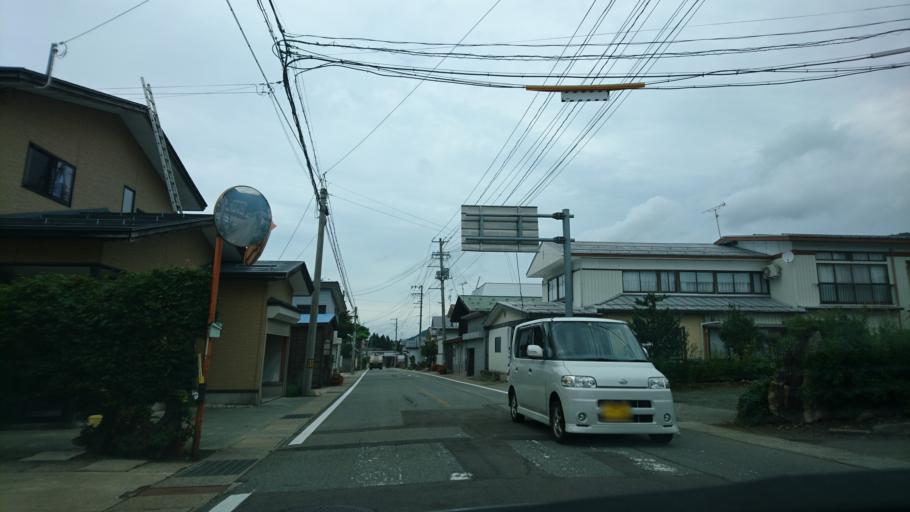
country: JP
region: Akita
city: Yuzawa
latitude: 39.1075
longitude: 140.5828
